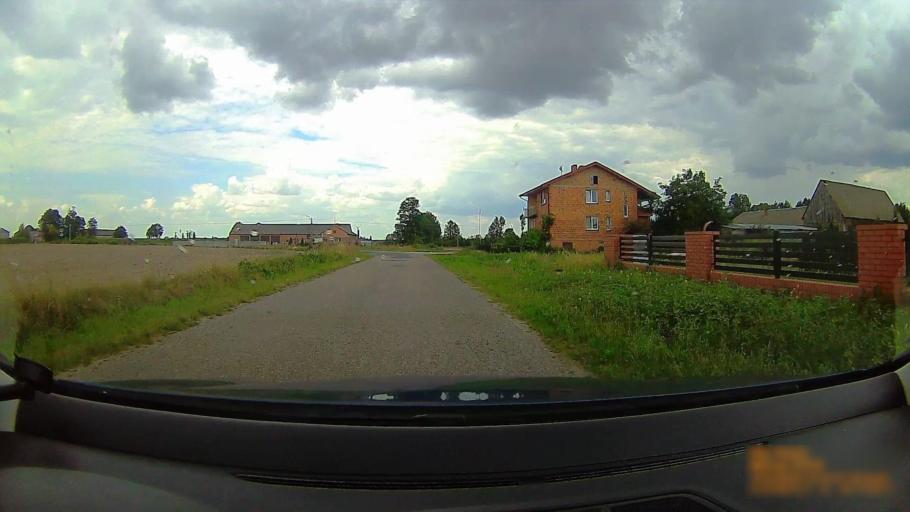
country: PL
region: Greater Poland Voivodeship
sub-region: Powiat koninski
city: Rychwal
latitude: 52.1061
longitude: 18.1903
